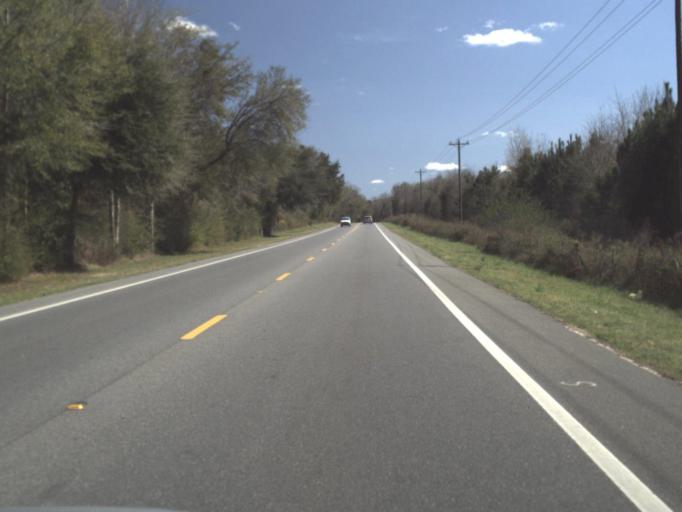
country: US
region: Florida
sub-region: Gadsden County
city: Gretna
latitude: 30.6000
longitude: -84.6510
